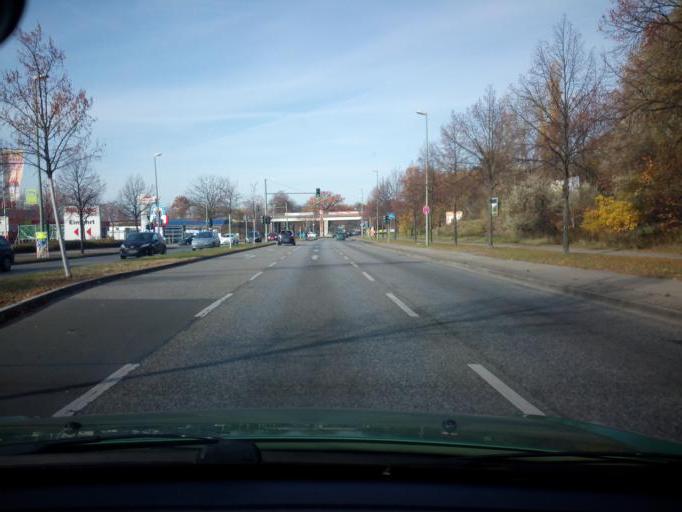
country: DE
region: Berlin
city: Biesdorf
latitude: 52.5070
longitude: 13.5666
